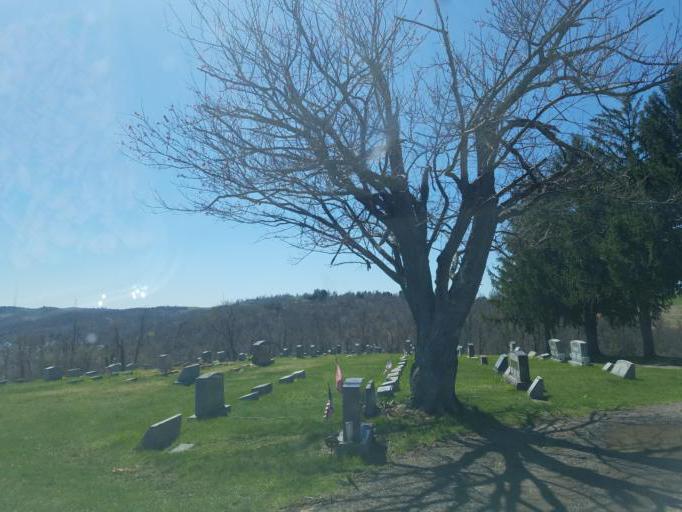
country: US
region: Ohio
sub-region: Belmont County
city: Martins Ferry
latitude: 40.1060
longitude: -80.7249
